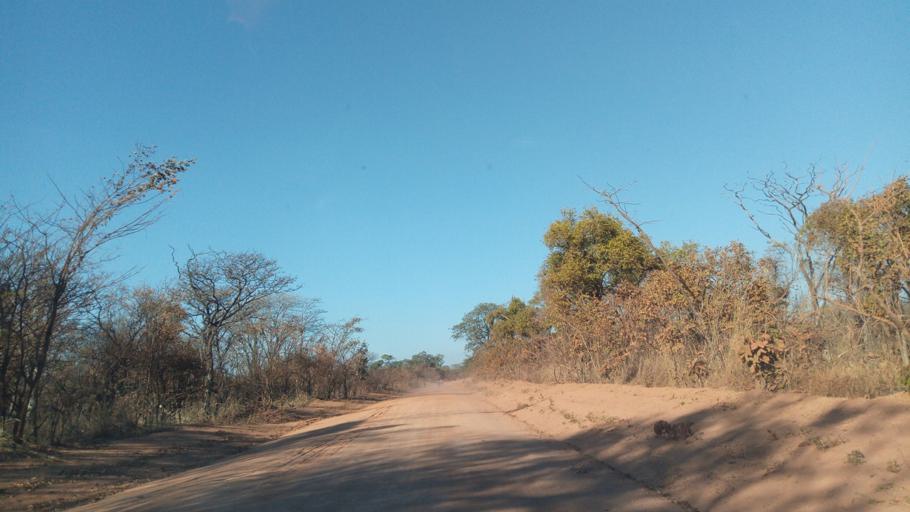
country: ZM
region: Luapula
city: Mwense
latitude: -10.5288
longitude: 28.4543
